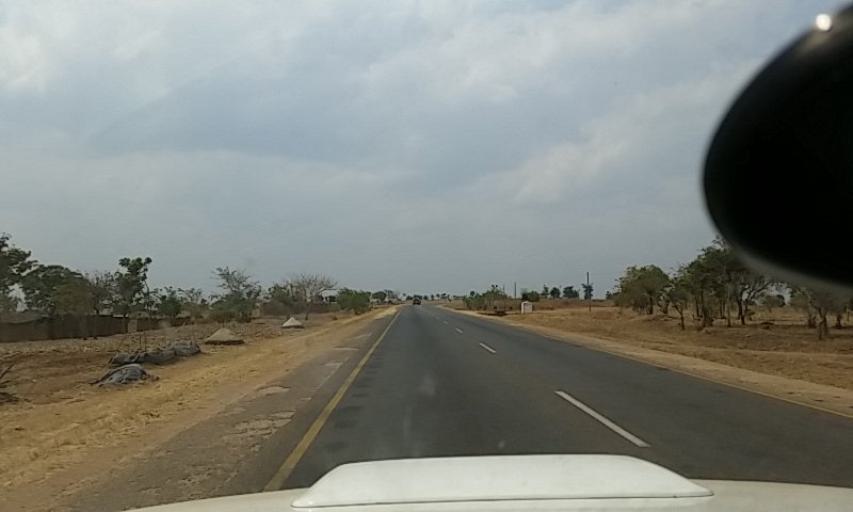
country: MW
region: Central Region
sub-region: Lilongwe District
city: Lilongwe
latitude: -13.8307
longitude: 33.8540
